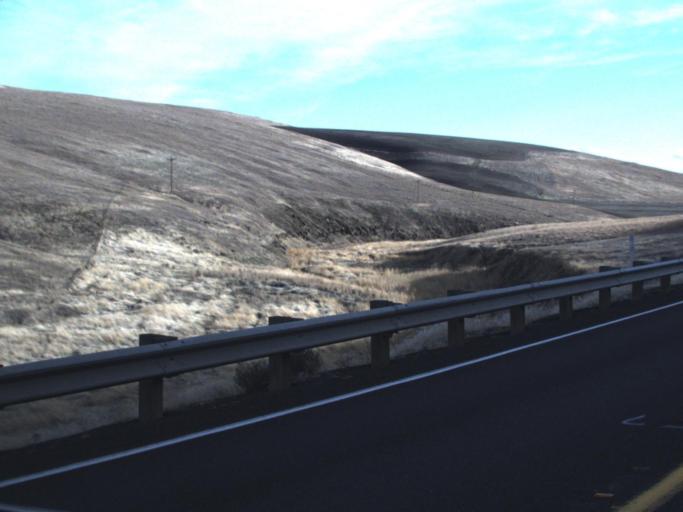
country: US
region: Washington
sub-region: Columbia County
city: Dayton
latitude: 46.4597
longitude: -117.9610
